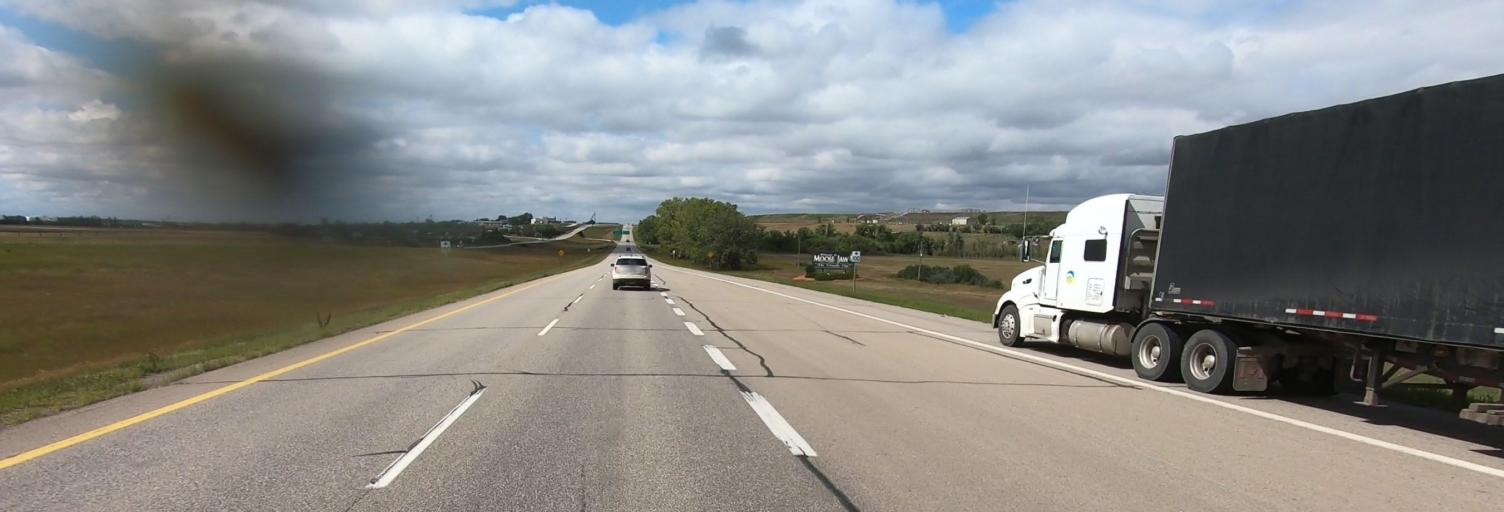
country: CA
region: Saskatchewan
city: Moose Jaw
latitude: 50.3940
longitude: -105.4698
